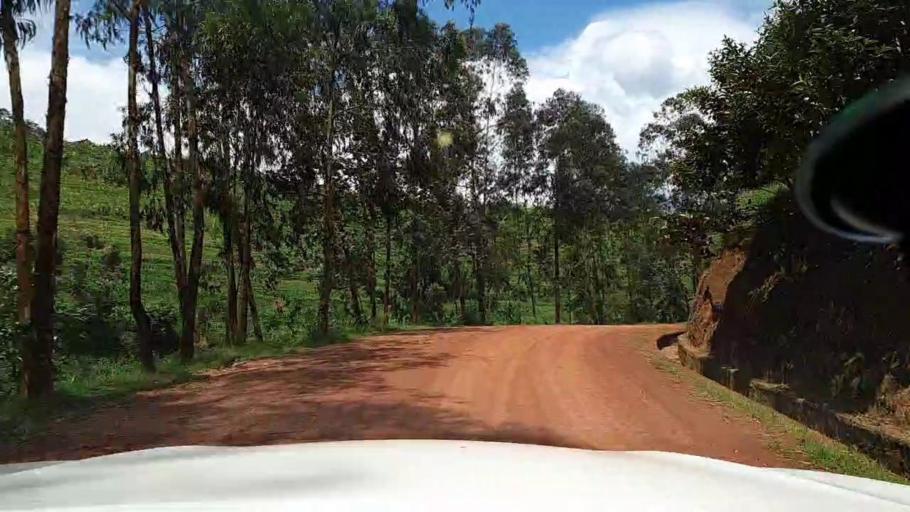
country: RW
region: Northern Province
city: Byumba
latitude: -1.6940
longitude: 29.8266
